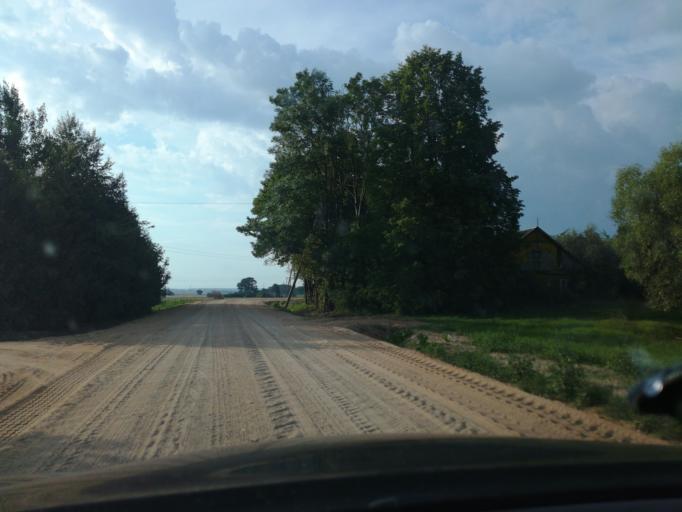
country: LT
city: Simnas
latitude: 54.3897
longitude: 23.8177
